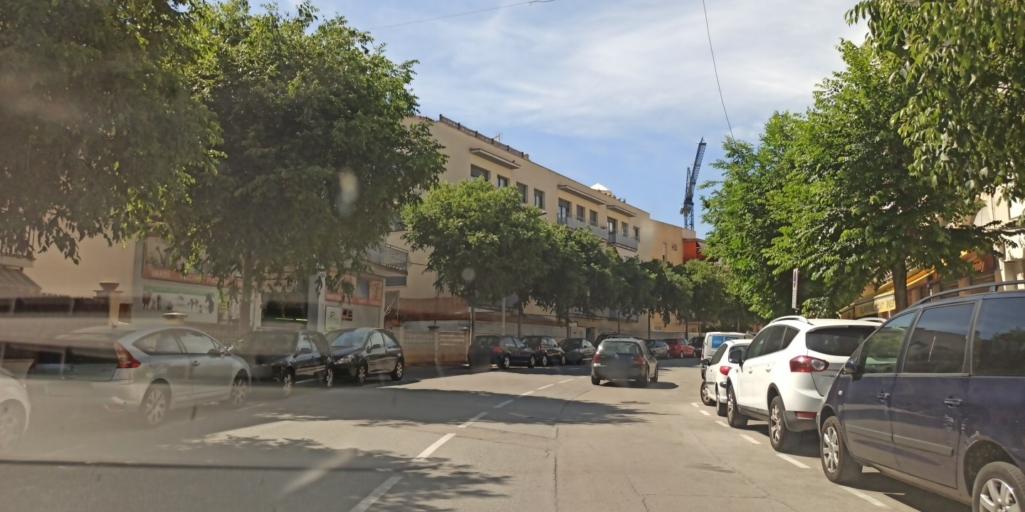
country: ES
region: Catalonia
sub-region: Provincia de Barcelona
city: Sant Pere de Ribes
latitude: 41.2598
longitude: 1.7741
